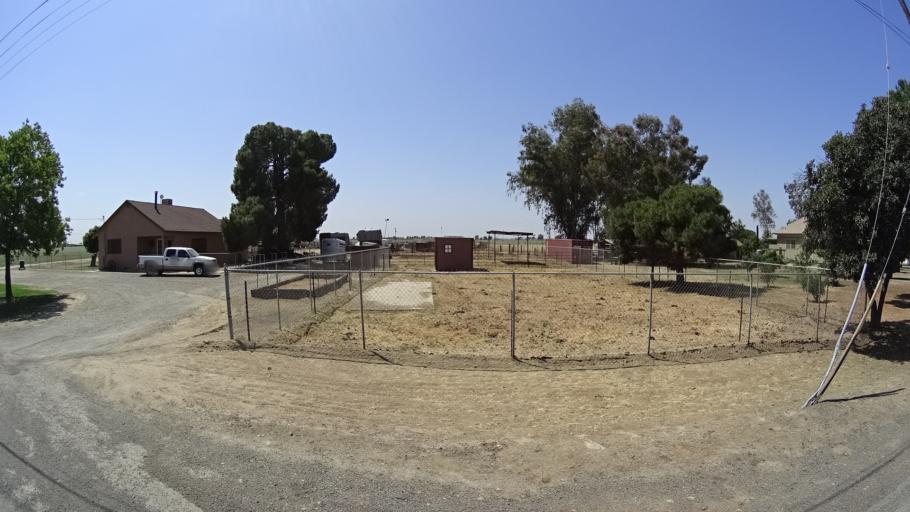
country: US
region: California
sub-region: Kings County
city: Home Garden
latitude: 36.2841
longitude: -119.6286
